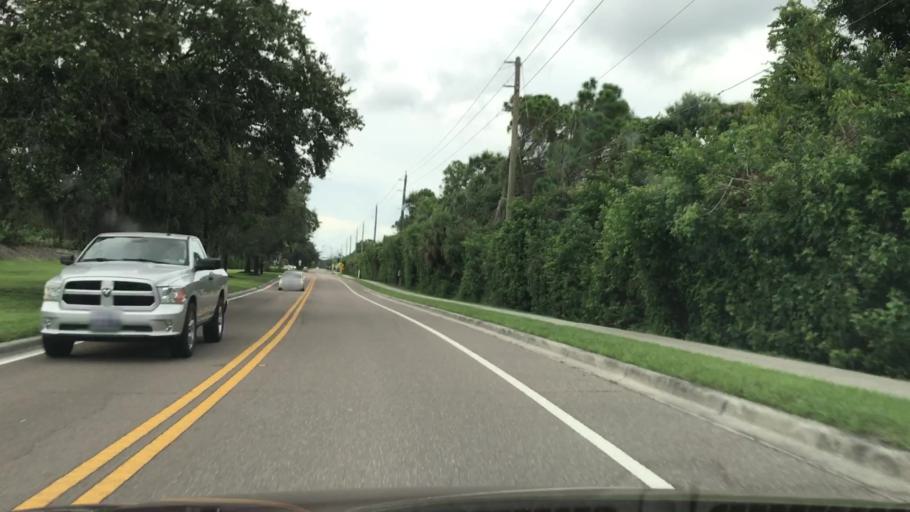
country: US
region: Florida
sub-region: Sarasota County
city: Vamo
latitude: 27.2411
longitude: -82.4738
